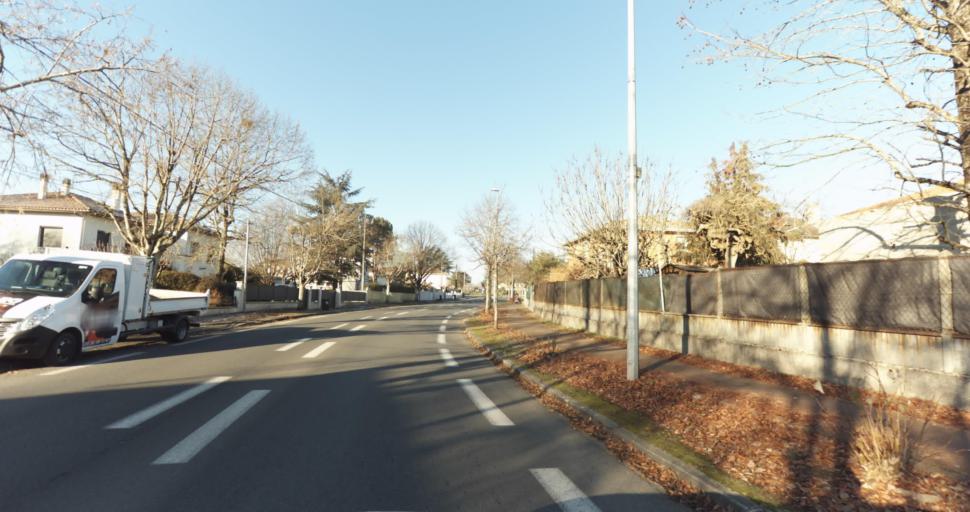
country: FR
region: Aquitaine
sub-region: Departement de la Gironde
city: Bassens
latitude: 44.8955
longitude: -0.5120
